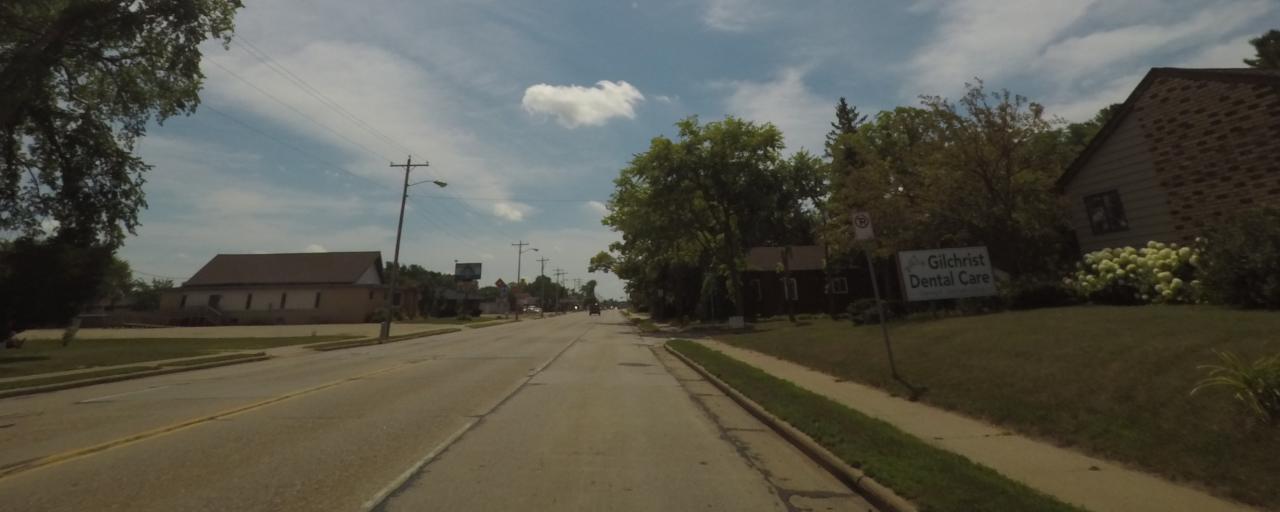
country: US
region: Wisconsin
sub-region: Portage County
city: Stevens Point
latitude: 44.5074
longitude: -89.5690
